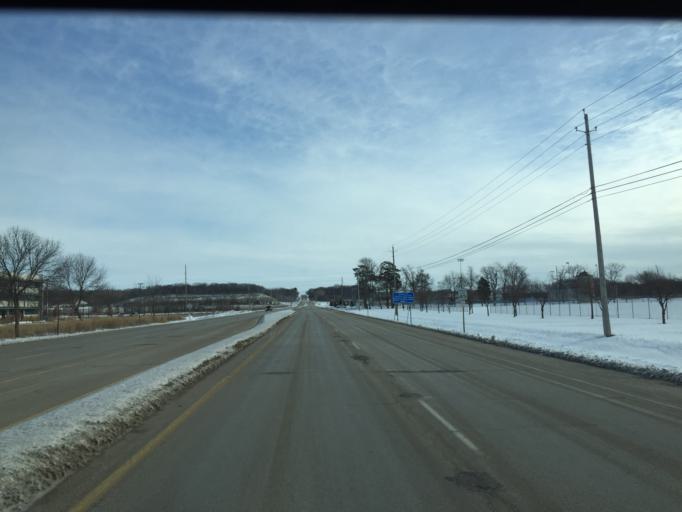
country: US
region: Minnesota
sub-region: Olmsted County
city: Rochester
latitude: 44.0215
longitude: -92.4324
